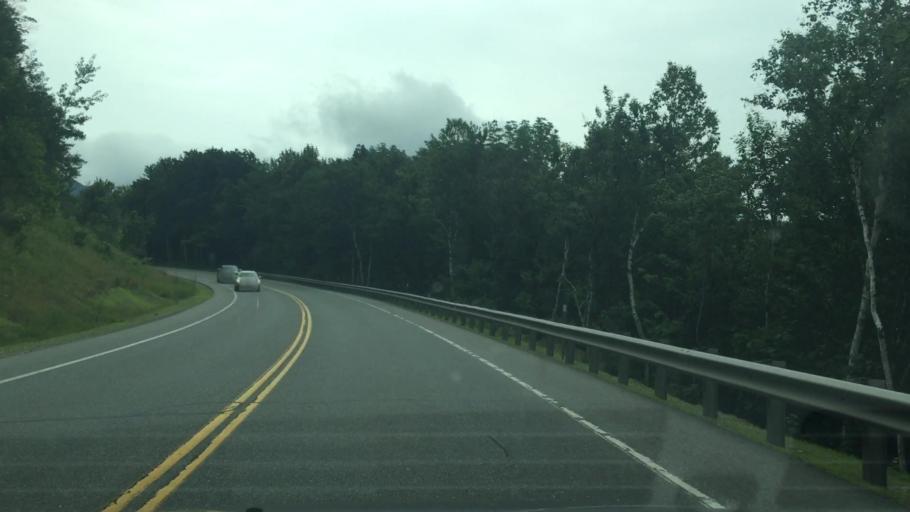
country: US
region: New Hampshire
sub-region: Grafton County
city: Deerfield
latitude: 44.2093
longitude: -71.6851
